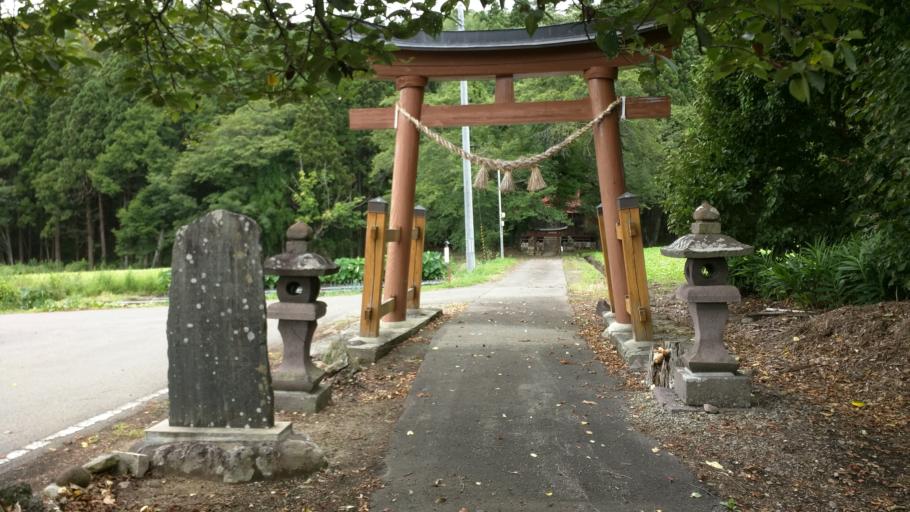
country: JP
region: Fukushima
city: Kitakata
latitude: 37.5822
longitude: 139.9455
